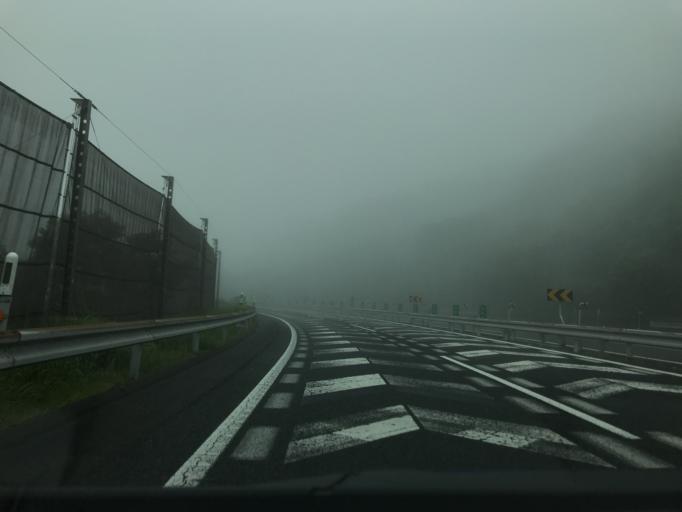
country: JP
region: Oita
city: Hiji
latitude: 33.3561
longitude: 131.4467
